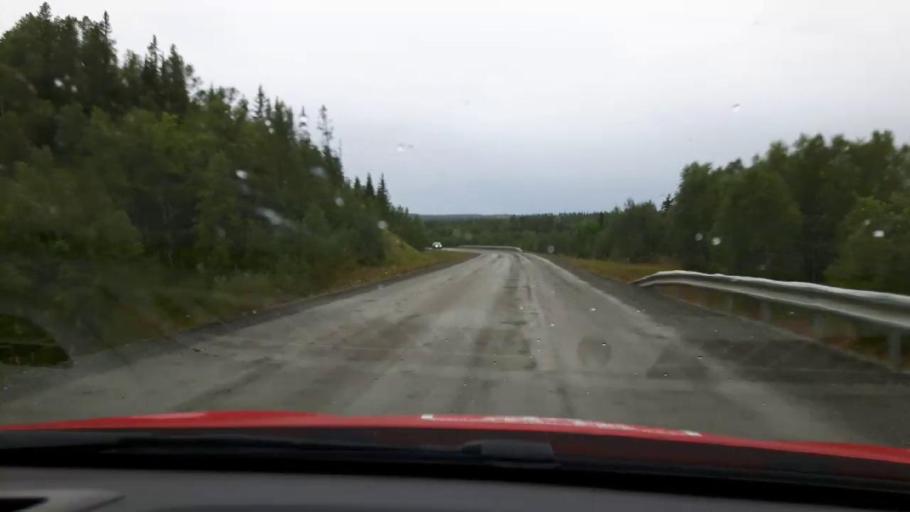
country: NO
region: Nord-Trondelag
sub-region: Meraker
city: Meraker
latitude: 63.5743
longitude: 12.2801
